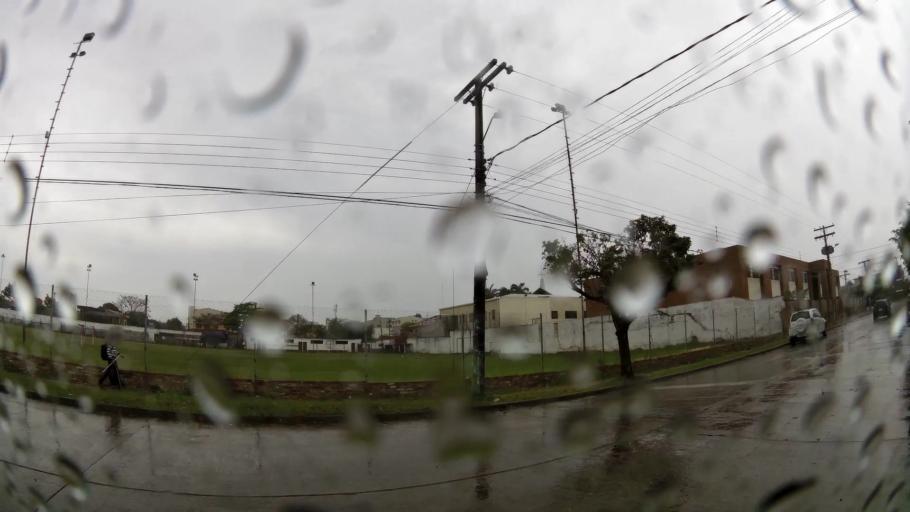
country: BO
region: Santa Cruz
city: Santa Cruz de la Sierra
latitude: -17.7841
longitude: -63.2014
